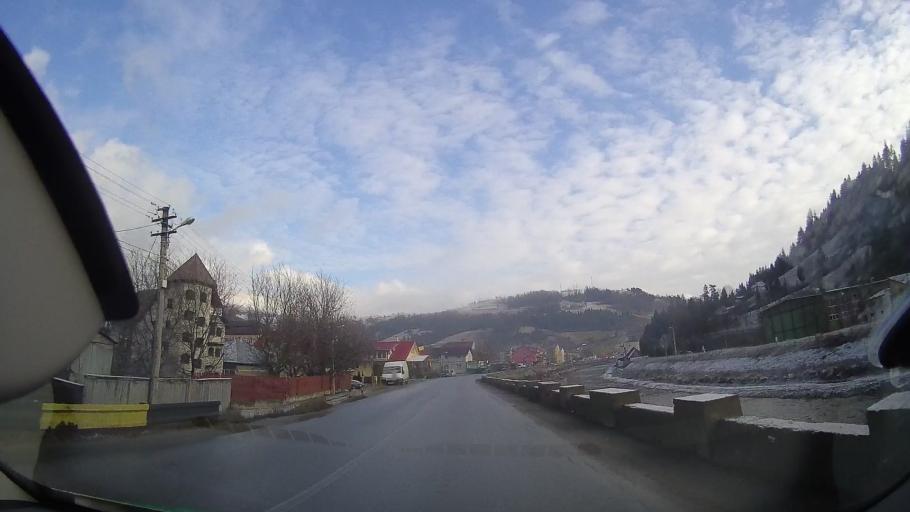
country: RO
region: Alba
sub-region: Oras Campeni
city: Campeni
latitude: 46.3601
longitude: 23.0459
